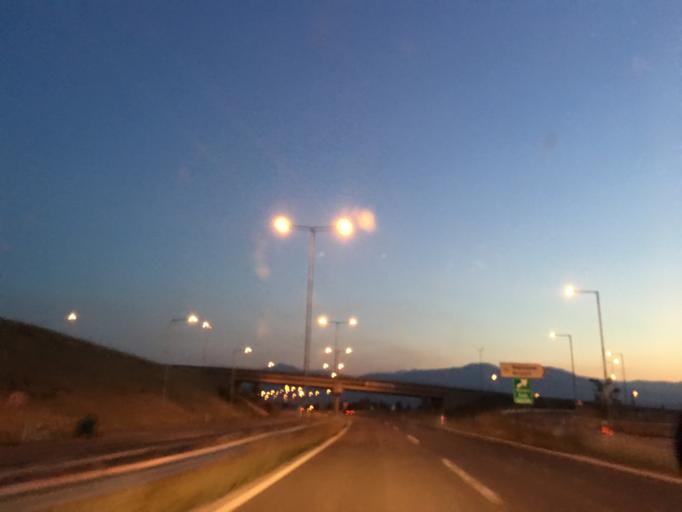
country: MK
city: Miladinovci
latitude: 41.9607
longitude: 21.6333
